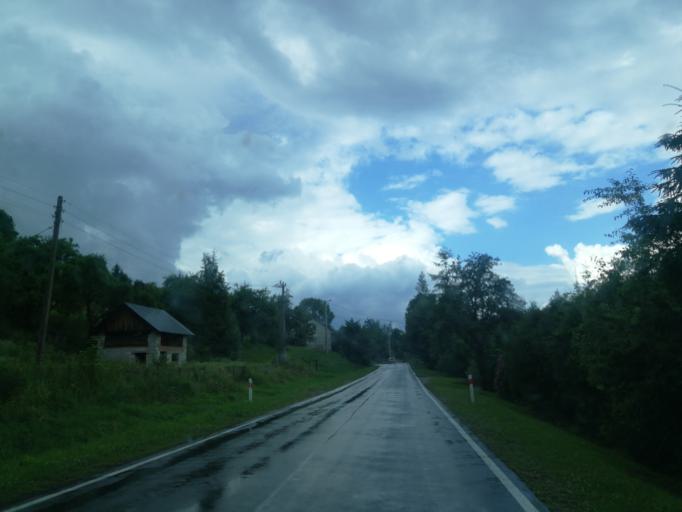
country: PL
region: Subcarpathian Voivodeship
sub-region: Powiat leski
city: Polanczyk
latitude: 49.4194
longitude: 22.4487
